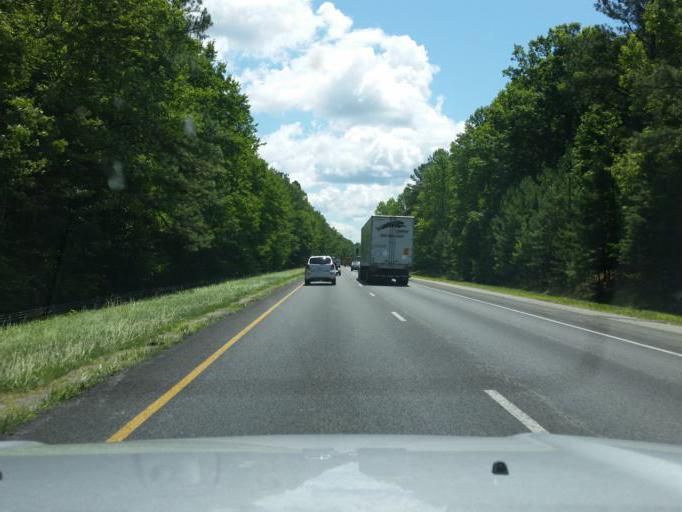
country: US
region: Virginia
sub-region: New Kent County
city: New Kent
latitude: 37.4768
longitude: -76.9158
